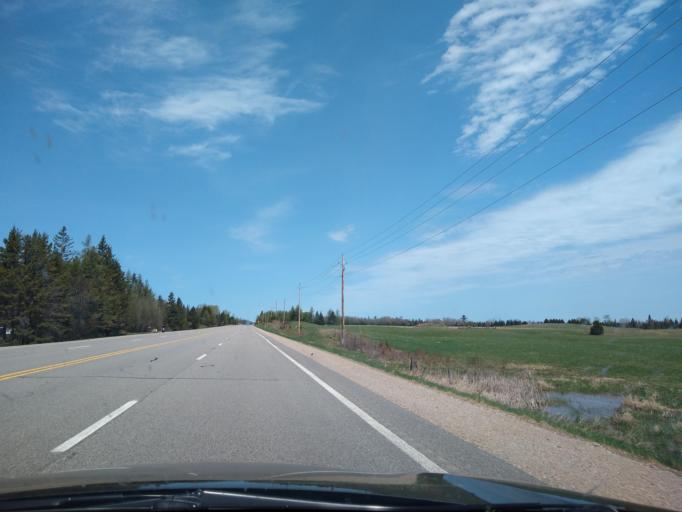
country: US
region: Michigan
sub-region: Delta County
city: Gladstone
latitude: 46.0879
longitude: -86.9807
